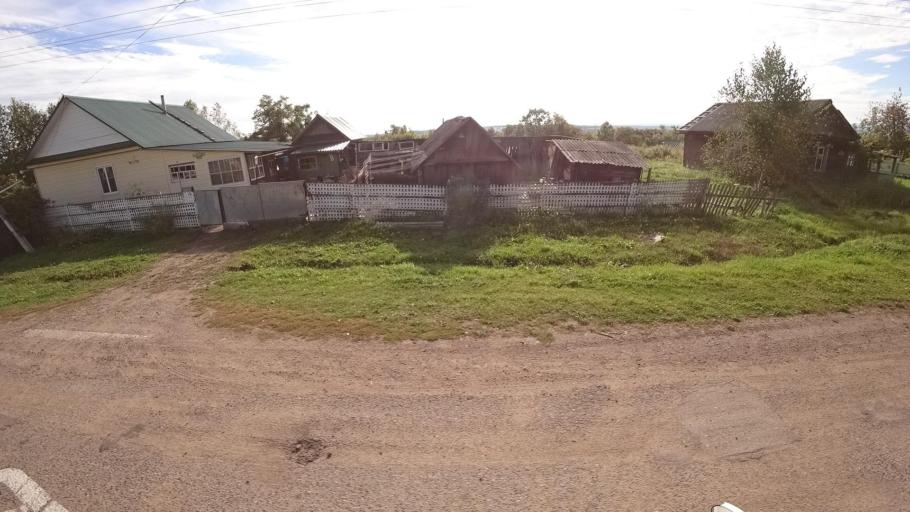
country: RU
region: Primorskiy
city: Dostoyevka
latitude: 44.2961
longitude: 133.4543
